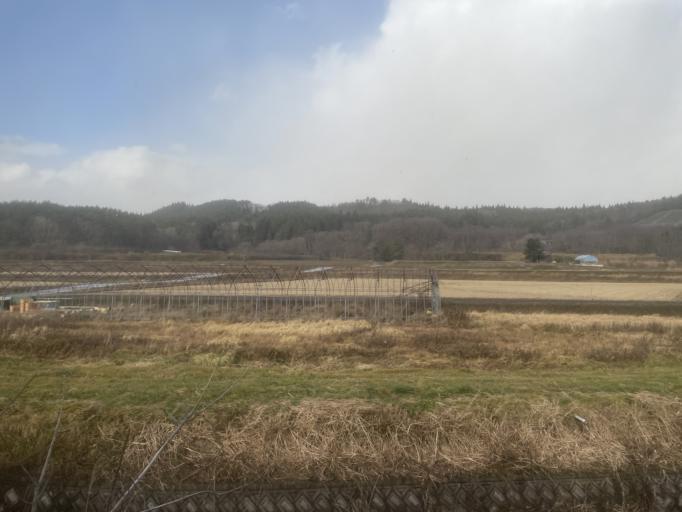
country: JP
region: Aomori
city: Goshogawara
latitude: 41.0658
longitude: 140.5587
